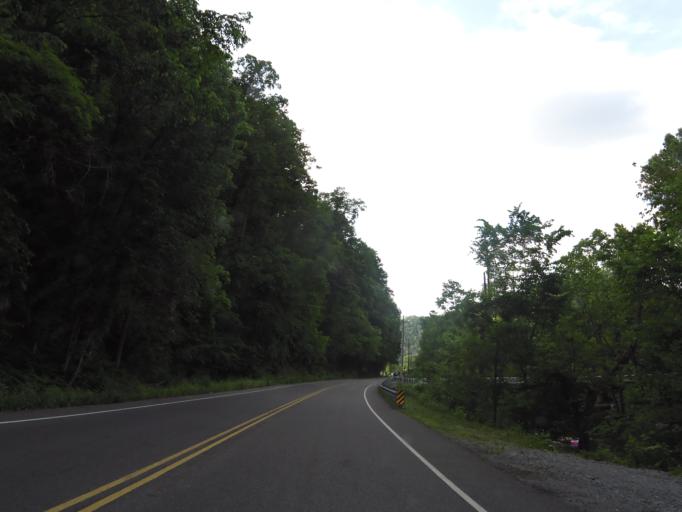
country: US
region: Tennessee
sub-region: Sevier County
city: Pigeon Forge
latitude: 35.6697
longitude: -83.7170
